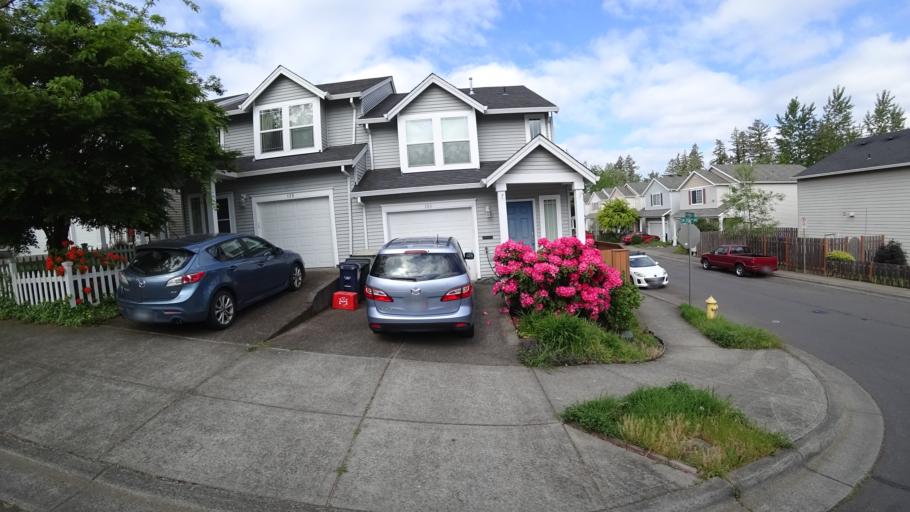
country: US
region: Oregon
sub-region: Washington County
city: Aloha
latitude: 45.5190
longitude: -122.8887
